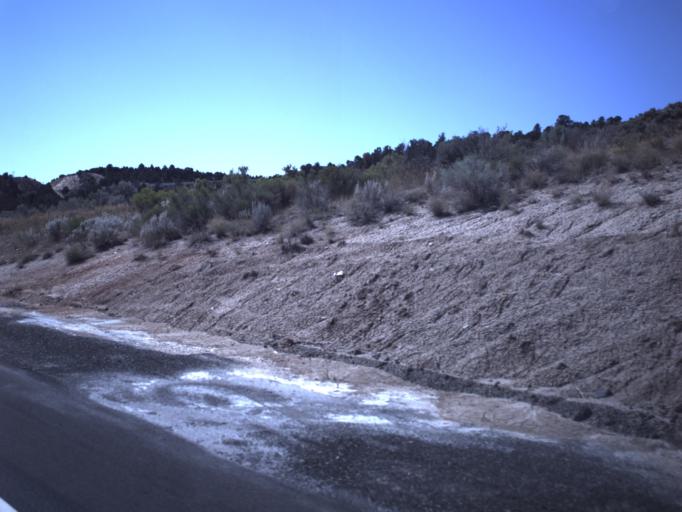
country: US
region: Utah
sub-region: Utah County
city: Eagle Mountain
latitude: 39.9964
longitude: -112.2716
